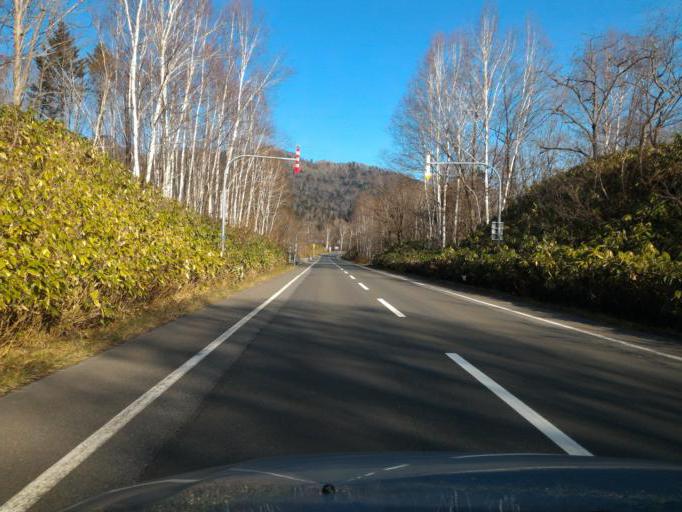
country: JP
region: Hokkaido
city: Ashibetsu
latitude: 43.3006
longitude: 142.1132
